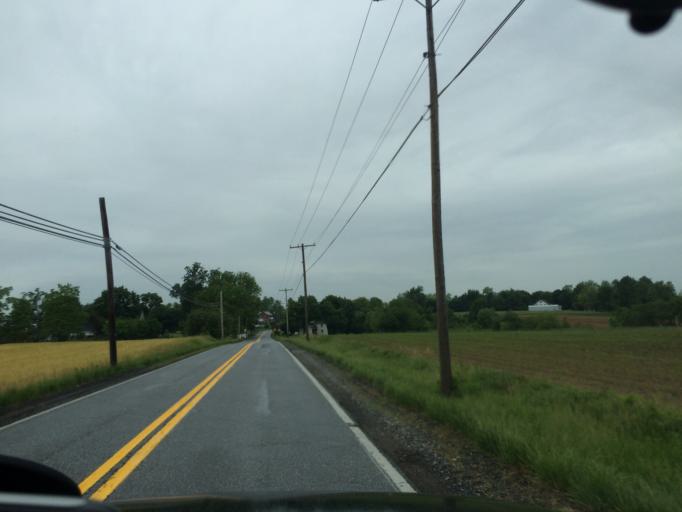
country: US
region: Maryland
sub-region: Carroll County
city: Taneytown
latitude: 39.5932
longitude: -77.1981
